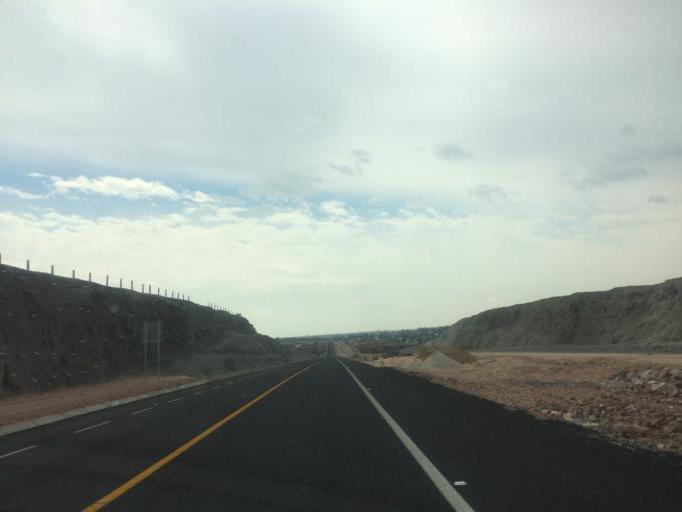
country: MX
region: Guanajuato
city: Duarte
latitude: 21.0618
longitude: -101.5345
